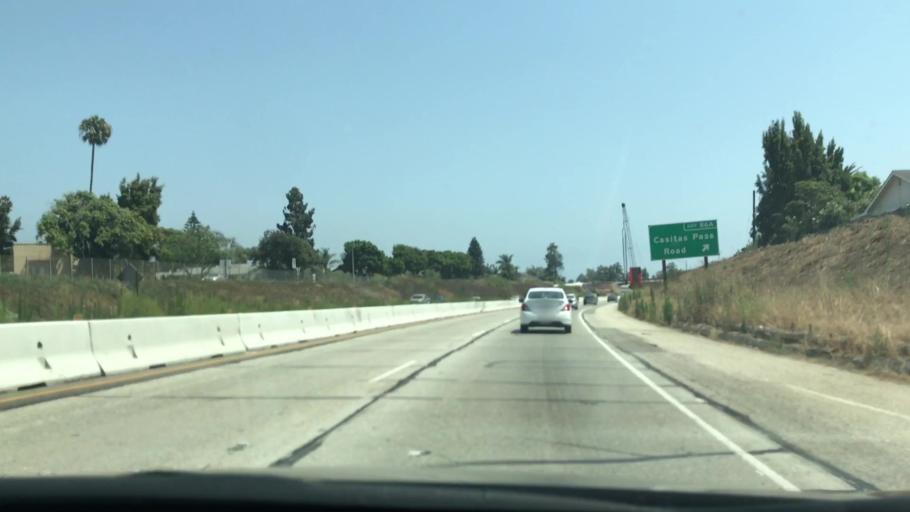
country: US
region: California
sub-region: Santa Barbara County
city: Carpinteria
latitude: 34.3998
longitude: -119.5143
